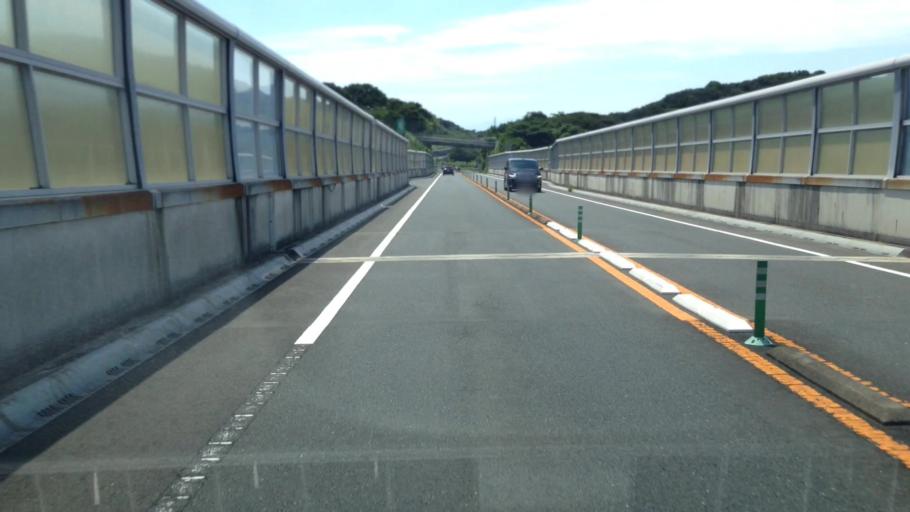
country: JP
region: Kanagawa
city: Yokosuka
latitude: 35.2322
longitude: 139.6483
